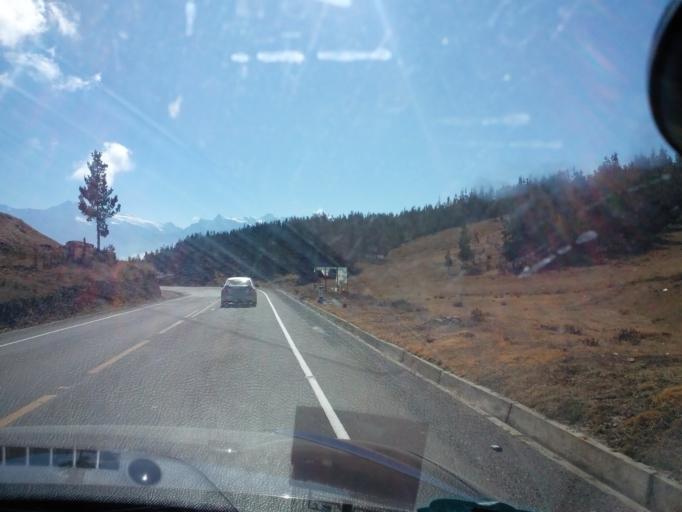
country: PE
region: Apurimac
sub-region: Provincia de Abancay
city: Cachora
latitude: -13.5677
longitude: -72.8217
